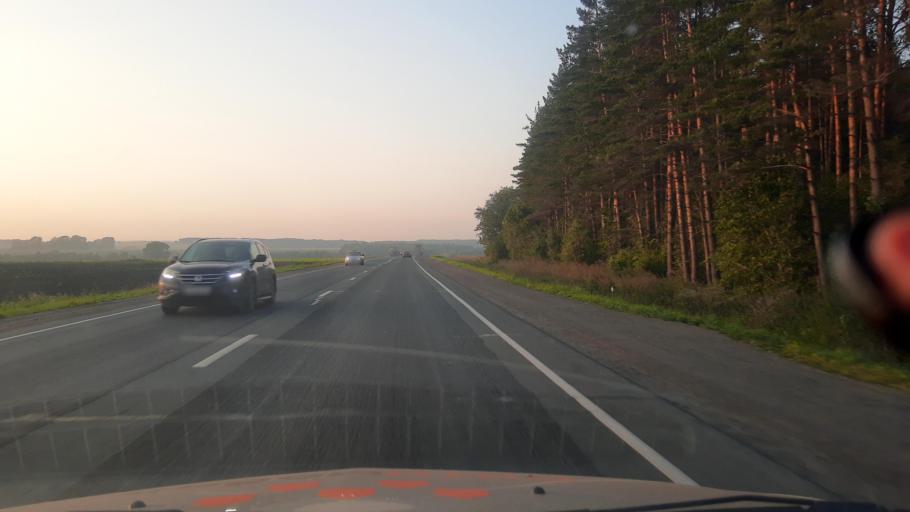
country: RU
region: Bashkortostan
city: Avdon
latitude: 54.7506
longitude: 55.7815
